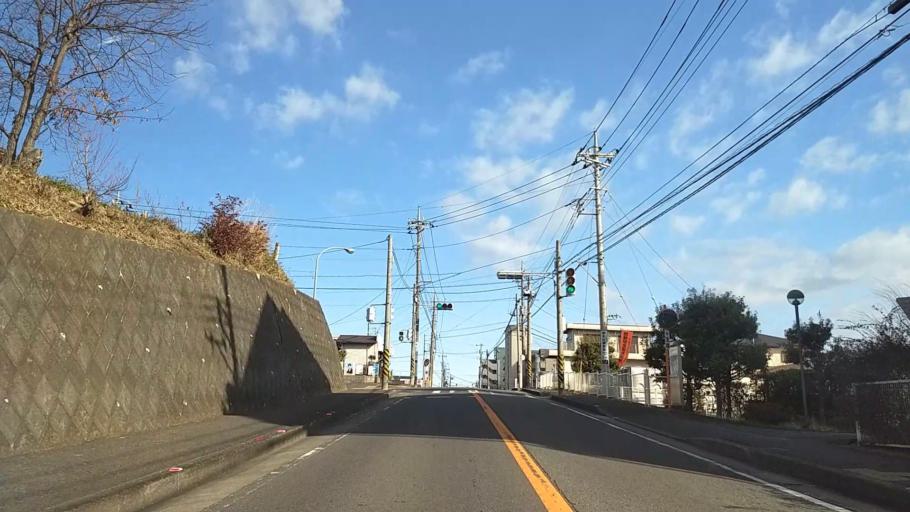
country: JP
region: Kanagawa
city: Atsugi
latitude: 35.4338
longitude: 139.3368
